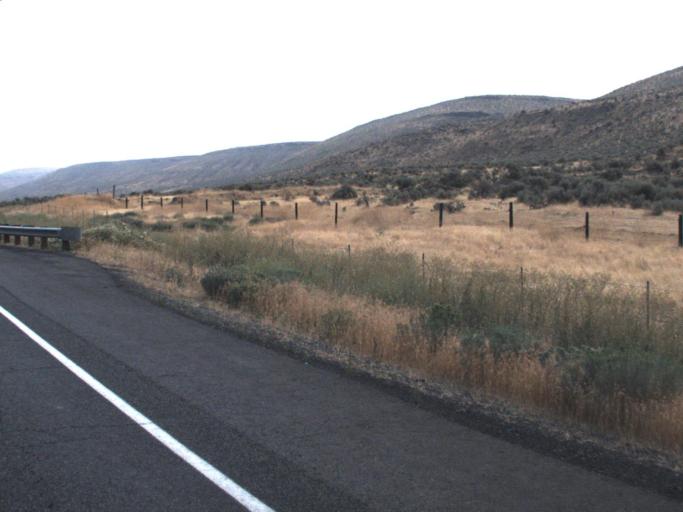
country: US
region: Washington
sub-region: Yakima County
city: Toppenish
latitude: 46.2116
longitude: -120.4581
